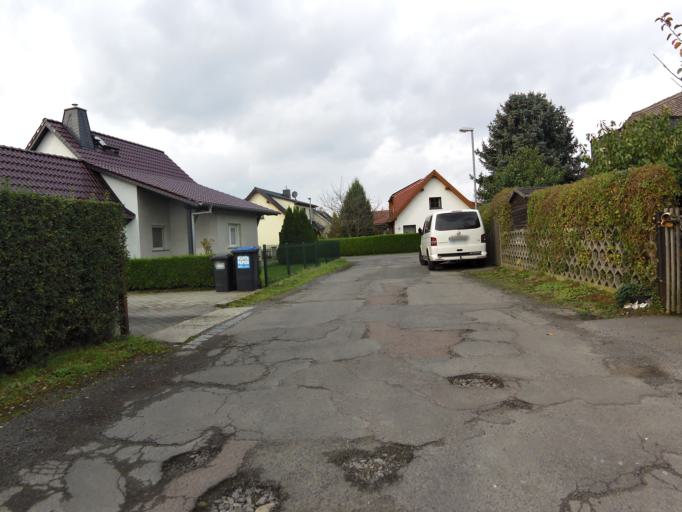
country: DE
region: Saxony
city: Taucha
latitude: 51.3898
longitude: 12.4382
